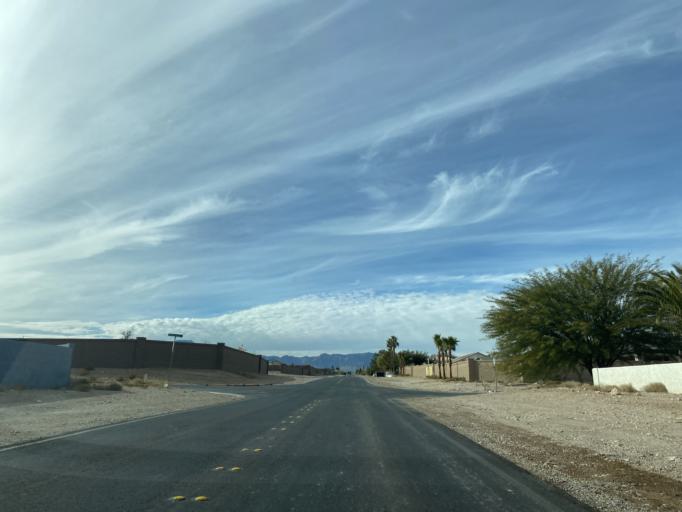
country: US
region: Nevada
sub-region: Clark County
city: Enterprise
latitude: 36.0338
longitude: -115.2536
